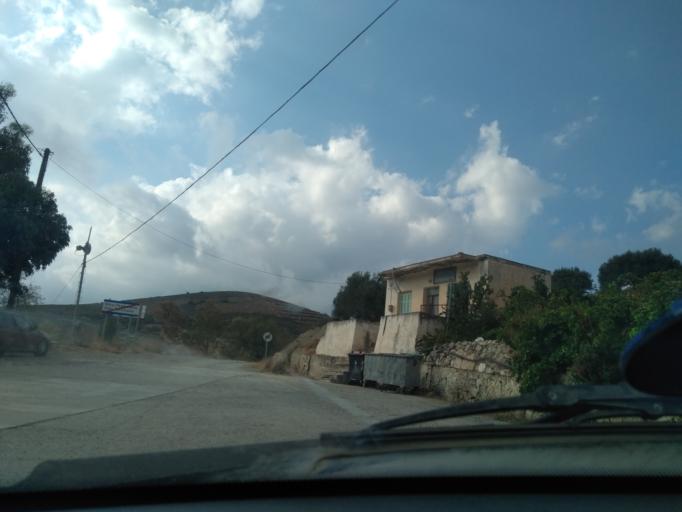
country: GR
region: Crete
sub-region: Nomos Lasithiou
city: Makry-Gialos
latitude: 35.0455
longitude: 26.0601
